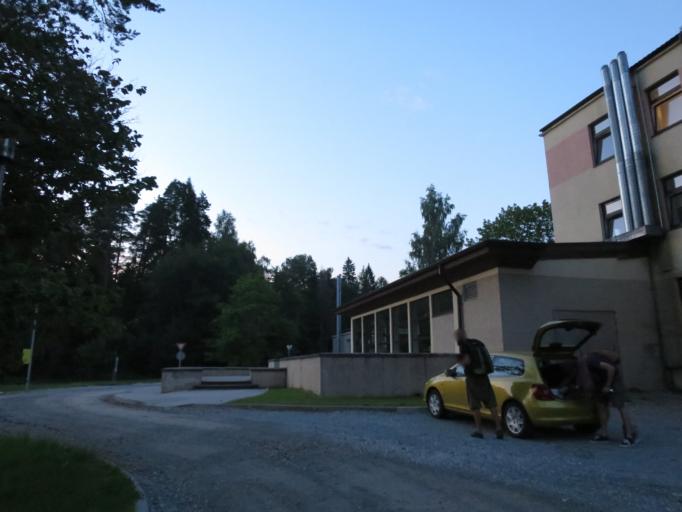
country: LV
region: Sigulda
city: Sigulda
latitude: 57.1402
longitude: 24.8175
